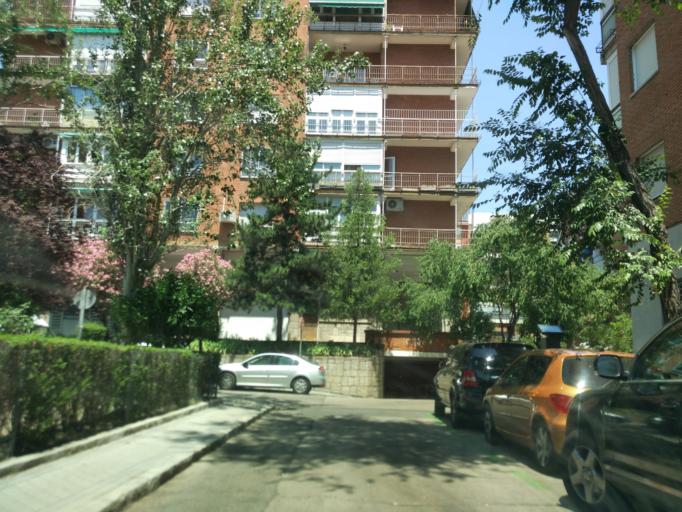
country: ES
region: Madrid
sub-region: Provincia de Madrid
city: Chamartin
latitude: 40.4730
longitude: -3.6887
